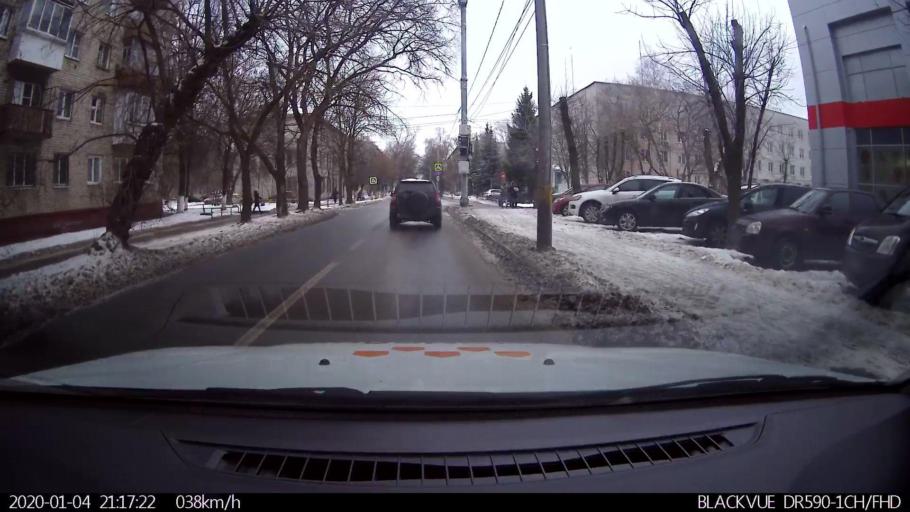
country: RU
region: Nizjnij Novgorod
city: Gorbatovka
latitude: 56.2344
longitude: 43.8527
